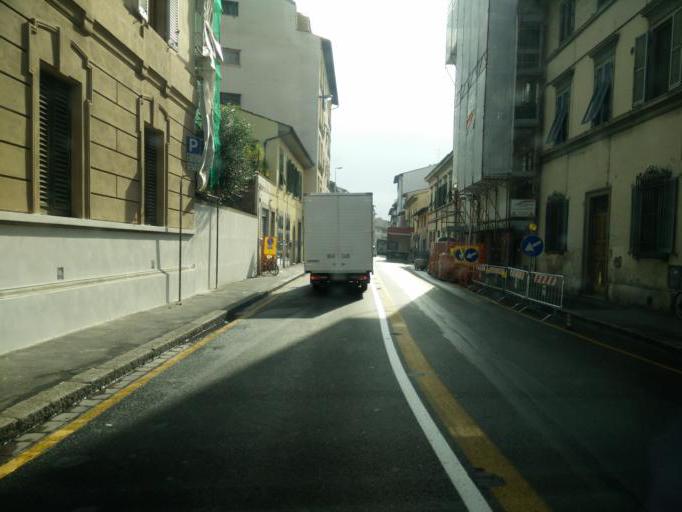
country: IT
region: Tuscany
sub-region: Province of Florence
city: Florence
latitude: 43.7831
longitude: 11.2337
